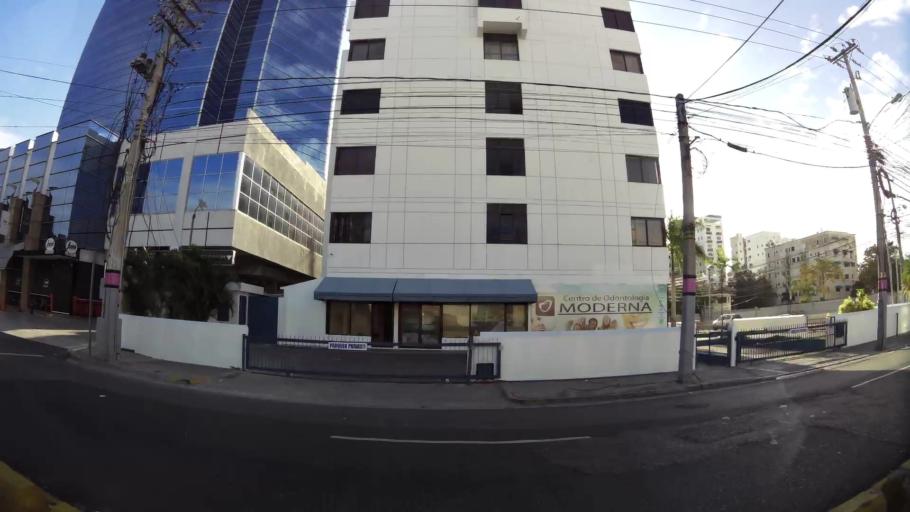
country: DO
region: Nacional
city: La Julia
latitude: 18.4726
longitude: -69.9315
